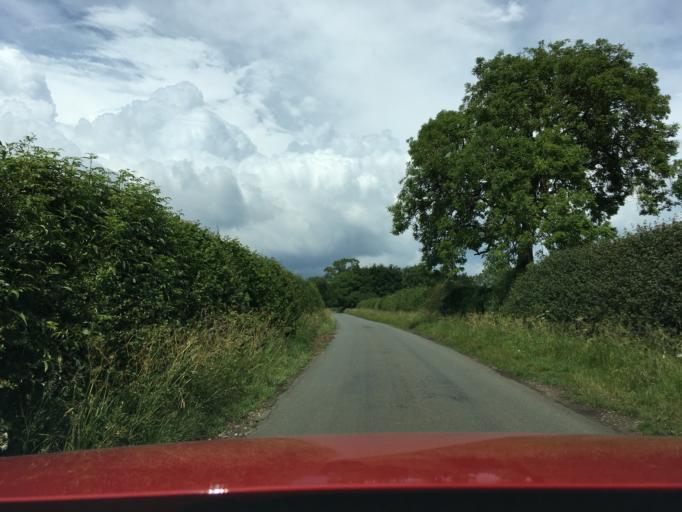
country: GB
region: England
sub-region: Gloucestershire
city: Chalford
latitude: 51.6907
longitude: -2.1286
